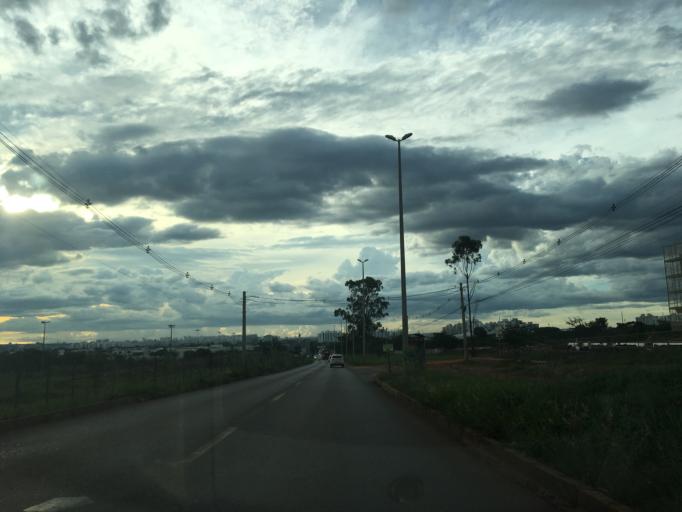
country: BR
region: Federal District
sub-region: Brasilia
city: Brasilia
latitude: -15.8327
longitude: -47.9442
